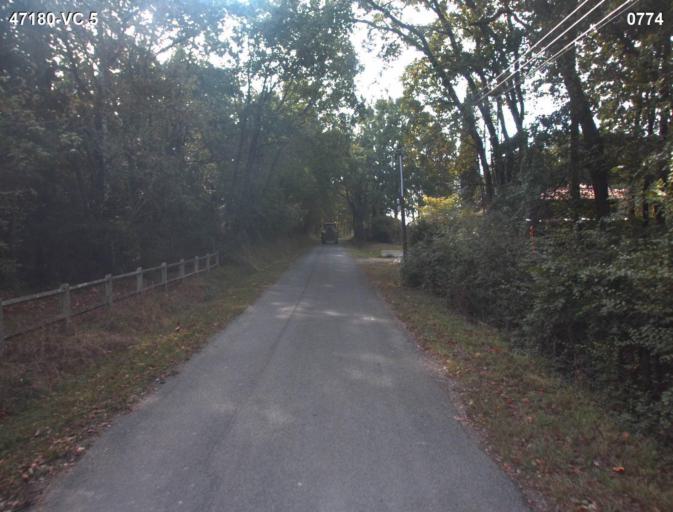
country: FR
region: Aquitaine
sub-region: Departement du Lot-et-Garonne
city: Sainte-Colombe-en-Bruilhois
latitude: 44.1760
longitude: 0.4680
